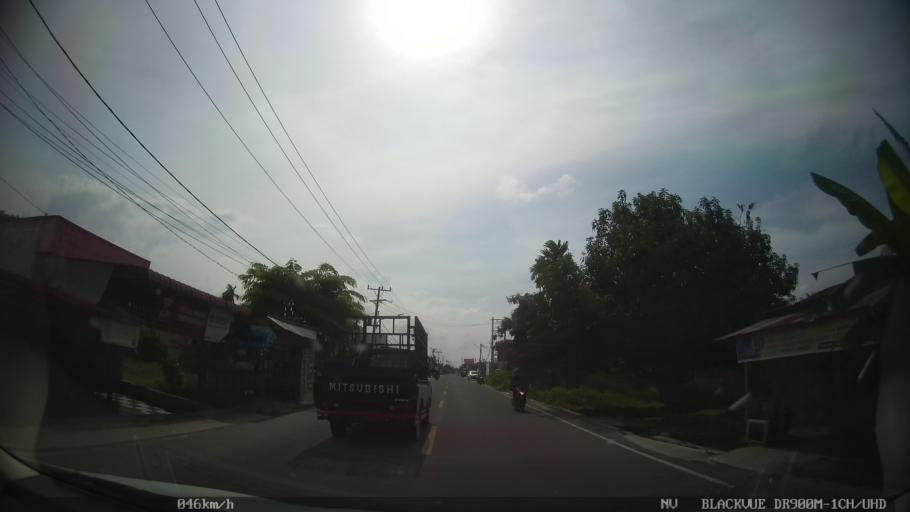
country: ID
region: North Sumatra
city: Percut
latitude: 3.6115
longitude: 98.8188
